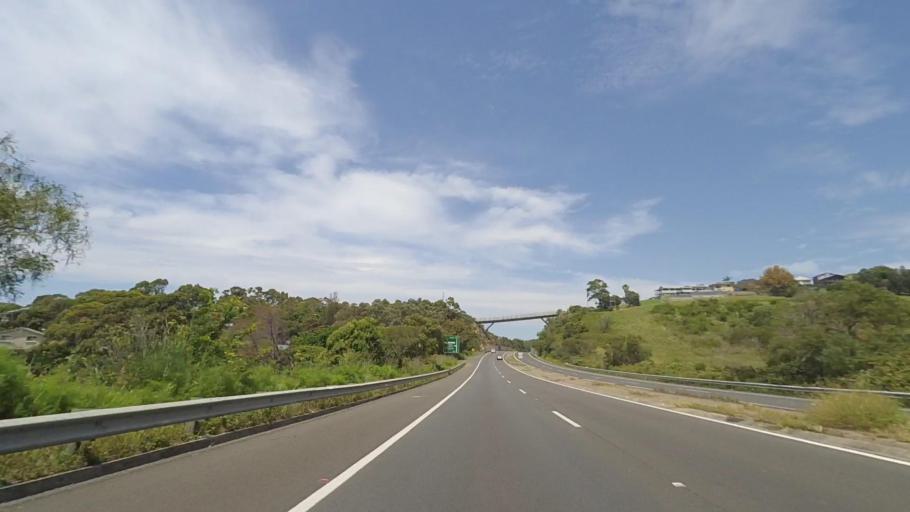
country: AU
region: New South Wales
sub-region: Kiama
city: Kiama
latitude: -34.6792
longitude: 150.8440
